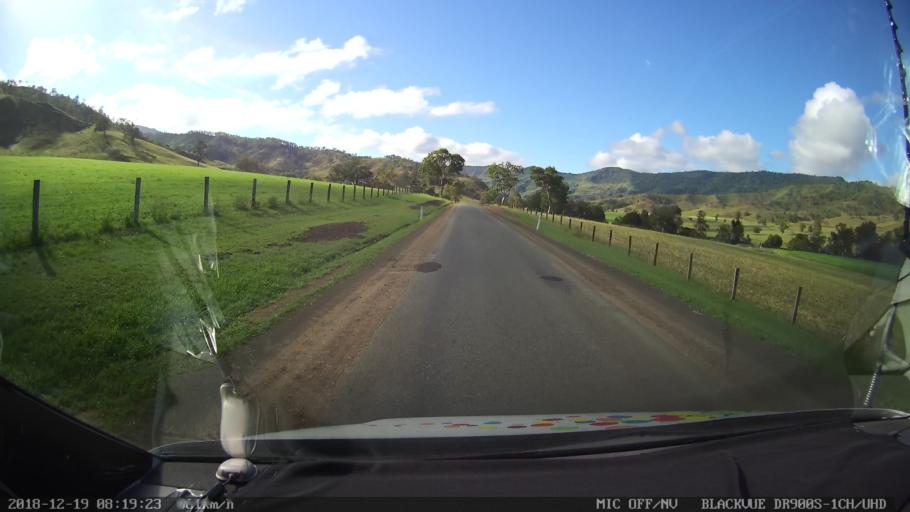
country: AU
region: New South Wales
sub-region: Kyogle
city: Kyogle
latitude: -28.2813
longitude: 152.9087
